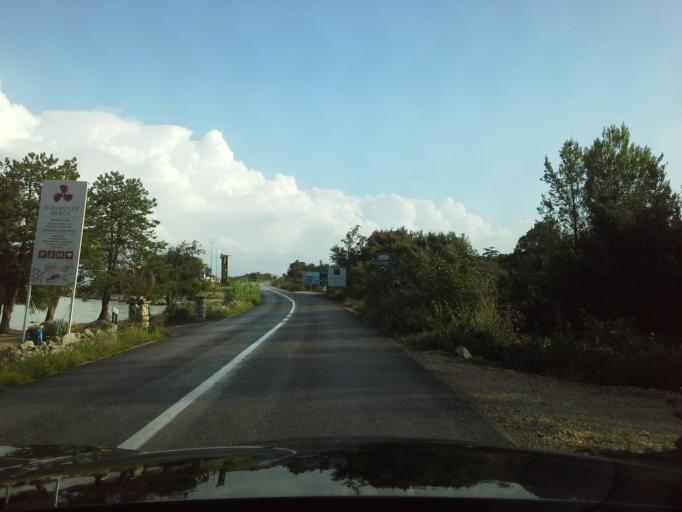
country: HR
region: Primorsko-Goranska
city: Mali Losinj
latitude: 44.6739
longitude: 14.3957
